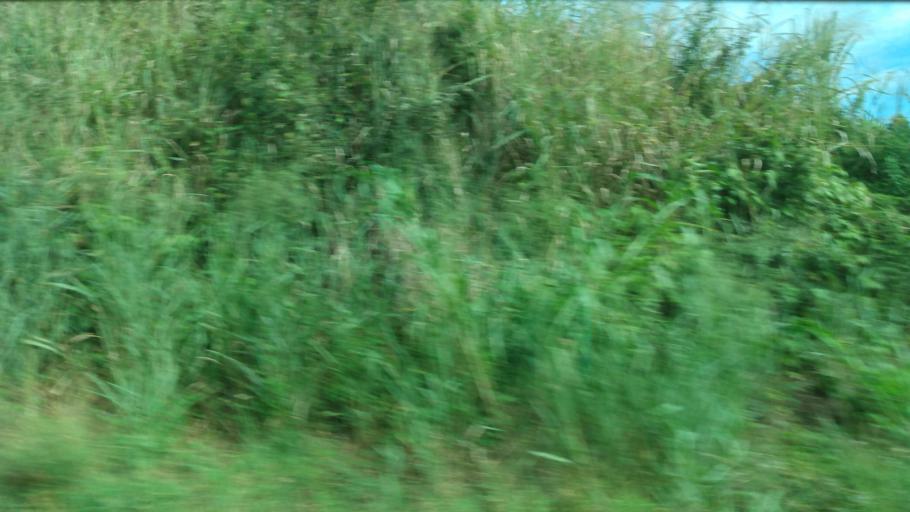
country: BR
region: Pernambuco
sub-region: Palmares
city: Palmares
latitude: -8.6948
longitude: -35.6485
